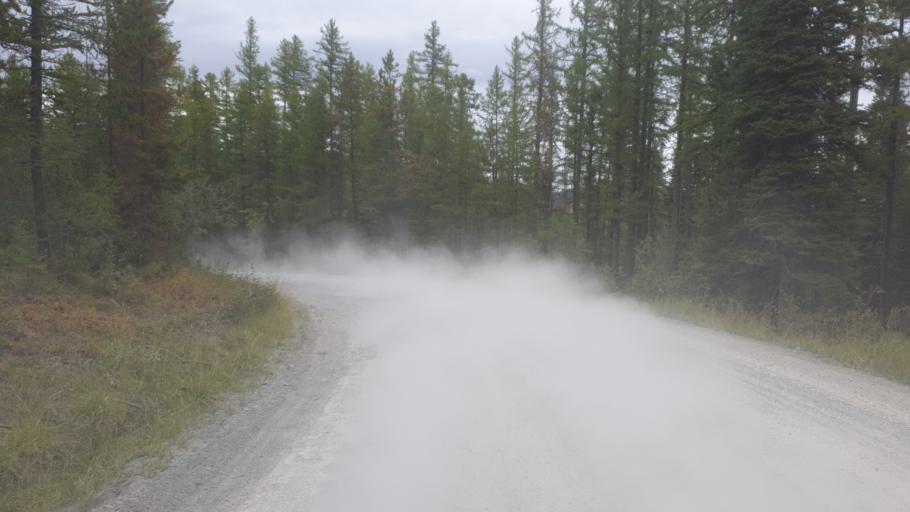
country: US
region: Montana
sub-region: Flathead County
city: Lakeside
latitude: 47.9901
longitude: -114.3233
